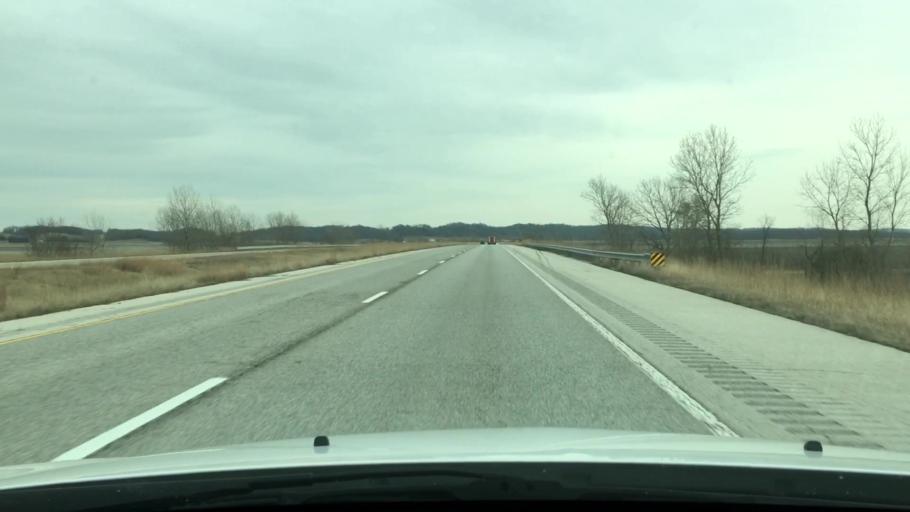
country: US
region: Illinois
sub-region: Pike County
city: Griggsville
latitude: 39.6886
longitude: -90.5987
